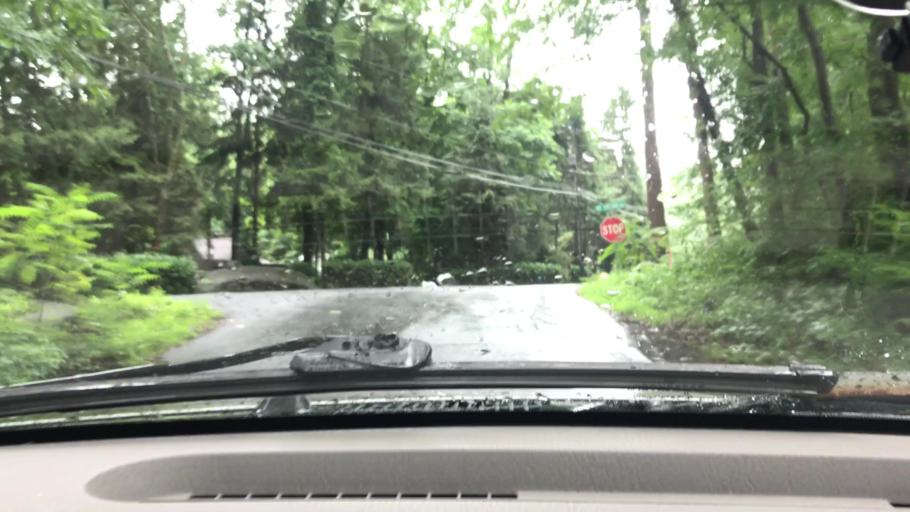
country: US
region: Pennsylvania
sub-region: Lancaster County
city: Elizabethtown
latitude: 40.1855
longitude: -76.5866
